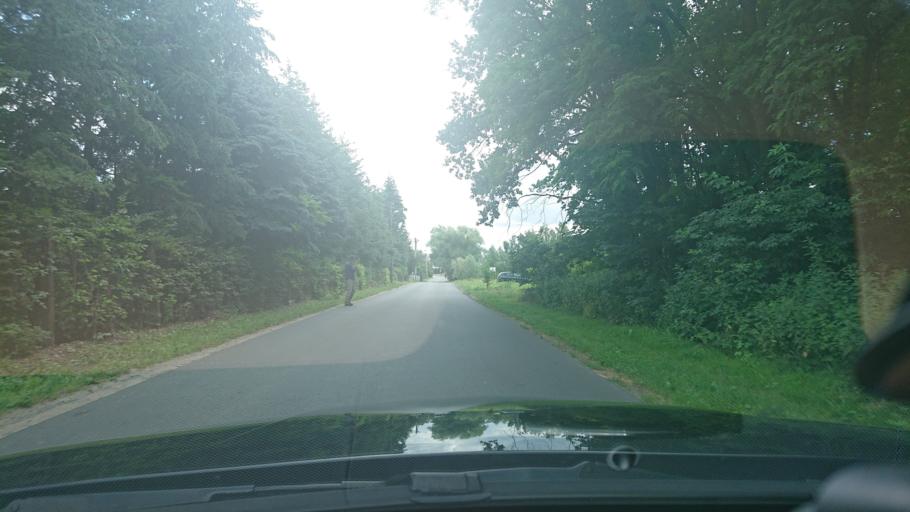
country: PL
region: Greater Poland Voivodeship
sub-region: Powiat gnieznienski
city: Gniezno
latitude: 52.5180
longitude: 17.6192
